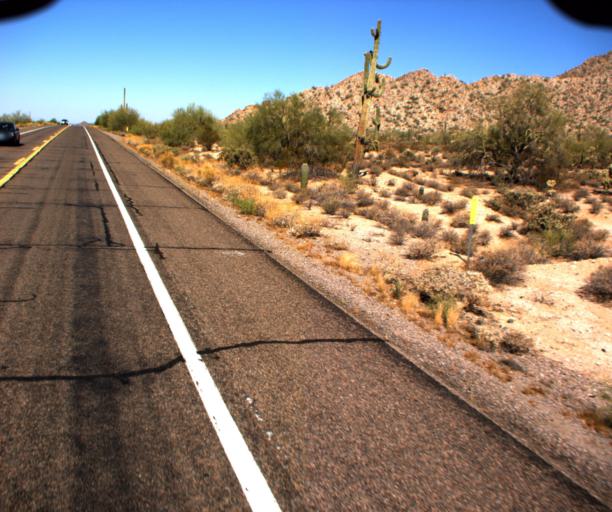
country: US
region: Arizona
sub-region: Pinal County
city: Sacaton
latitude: 33.0102
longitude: -111.6928
